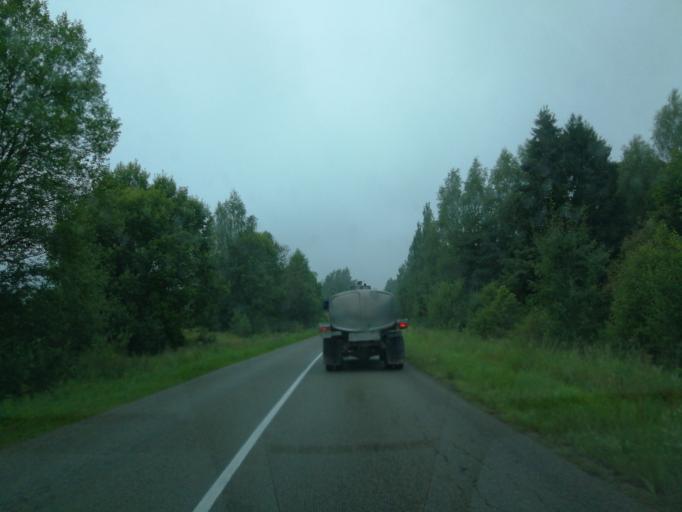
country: LV
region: Preilu Rajons
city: Jaunaglona
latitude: 56.2595
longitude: 26.9997
